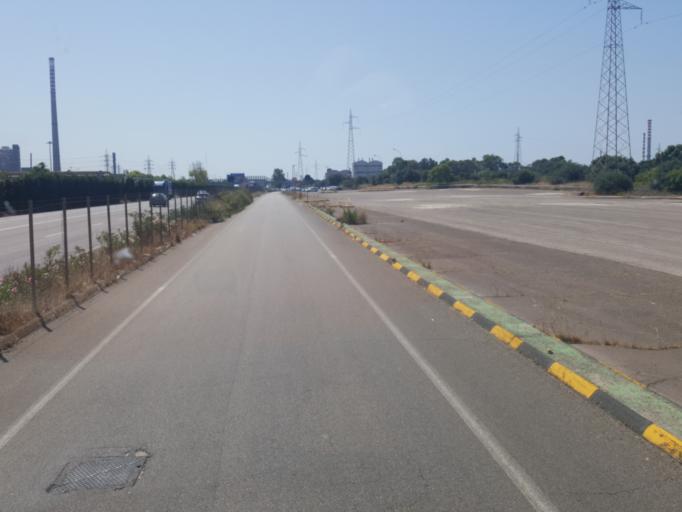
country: IT
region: Apulia
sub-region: Provincia di Taranto
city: Statte
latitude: 40.5070
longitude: 17.1950
